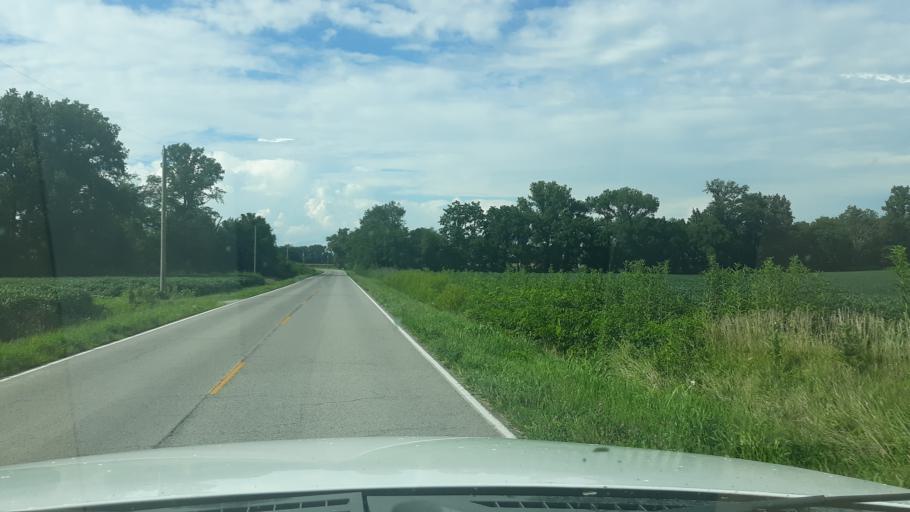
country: US
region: Illinois
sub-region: Saline County
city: Eldorado
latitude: 37.8585
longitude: -88.5304
